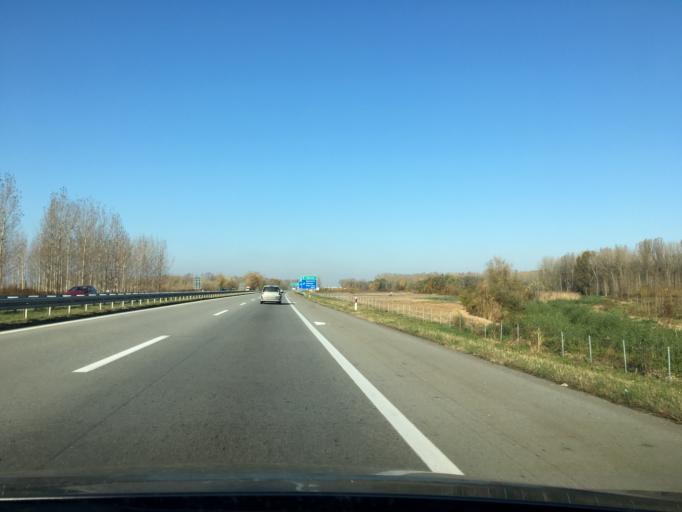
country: RS
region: Autonomna Pokrajina Vojvodina
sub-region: Juznobacki Okrug
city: Petrovaradin
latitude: 45.2819
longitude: 19.9037
